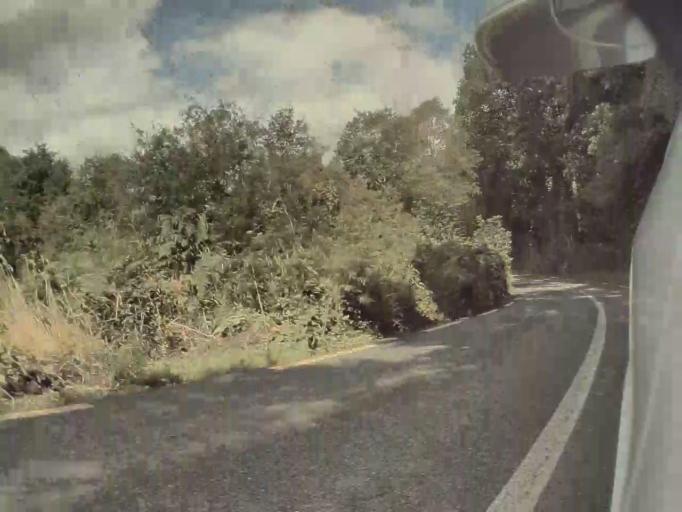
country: IE
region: Leinster
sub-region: Wicklow
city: Rathdrum
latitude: 53.0406
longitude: -6.2480
